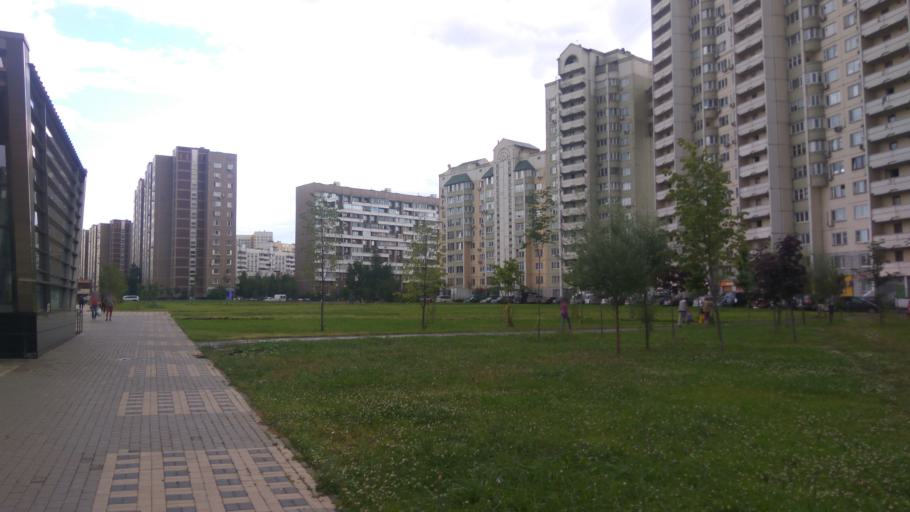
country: RU
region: Moscow
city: Zhulebino
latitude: 55.6840
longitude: 37.8555
